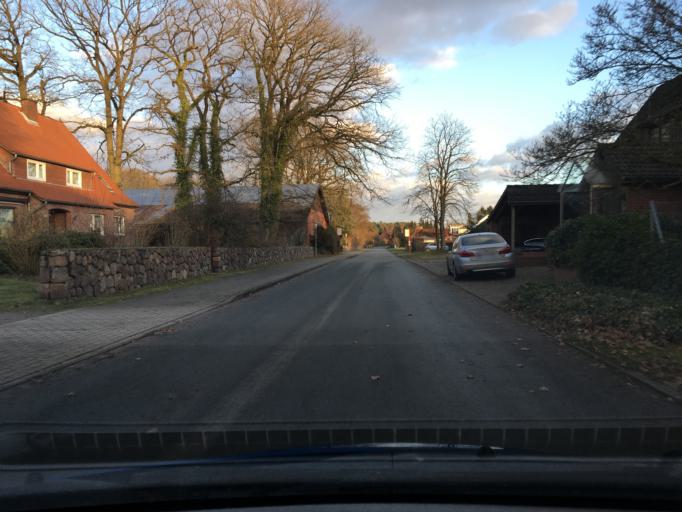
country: DE
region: Lower Saxony
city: Soderstorf
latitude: 53.1267
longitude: 10.1691
